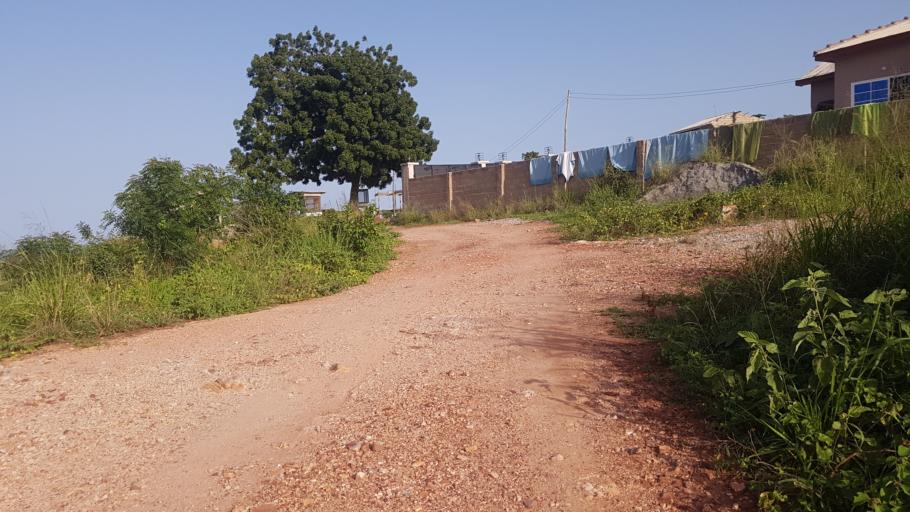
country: GH
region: Greater Accra
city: Gbawe
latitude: 5.5198
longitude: -0.3385
